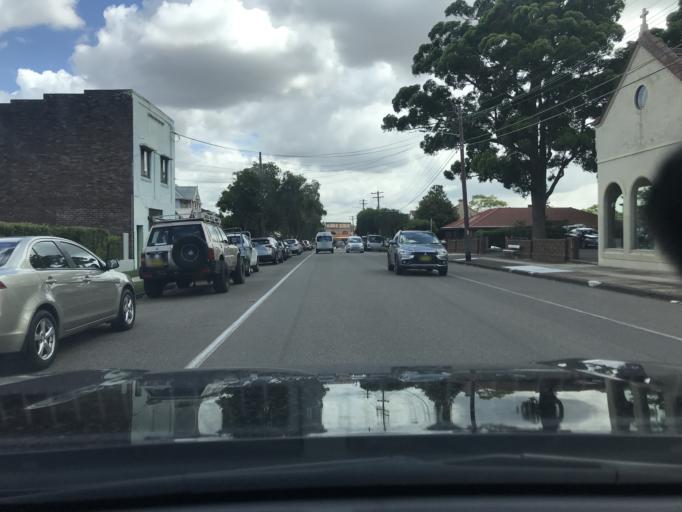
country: AU
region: New South Wales
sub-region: Canada Bay
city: Concord
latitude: -33.8469
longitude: 151.1074
